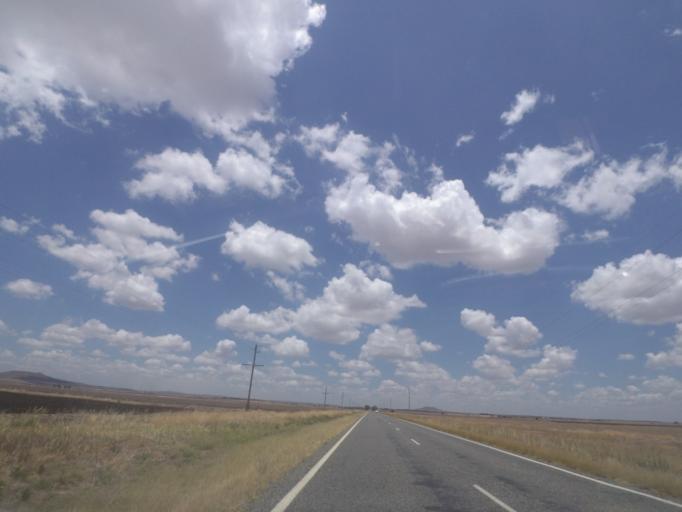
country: AU
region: Queensland
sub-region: Toowoomba
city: Top Camp
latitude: -27.9070
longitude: 151.9783
